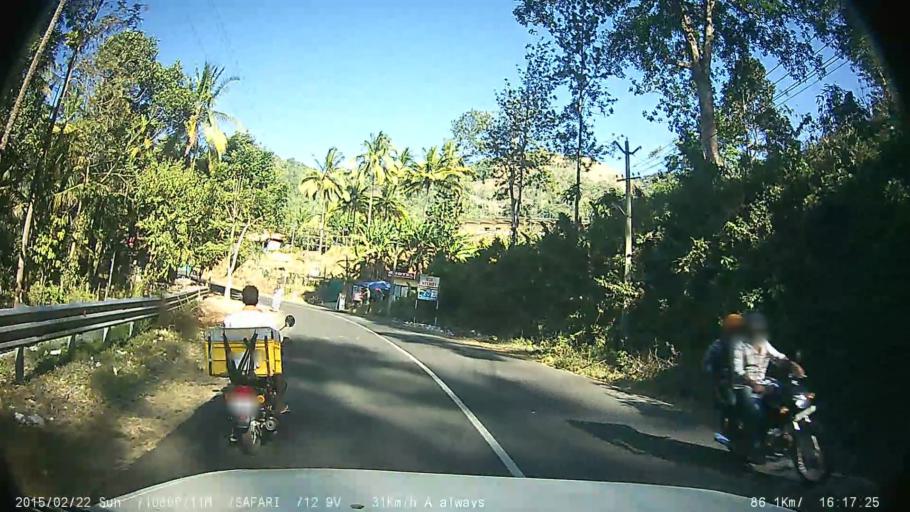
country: IN
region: Tamil Nadu
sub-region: Theni
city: Gudalur
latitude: 9.5825
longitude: 77.1165
